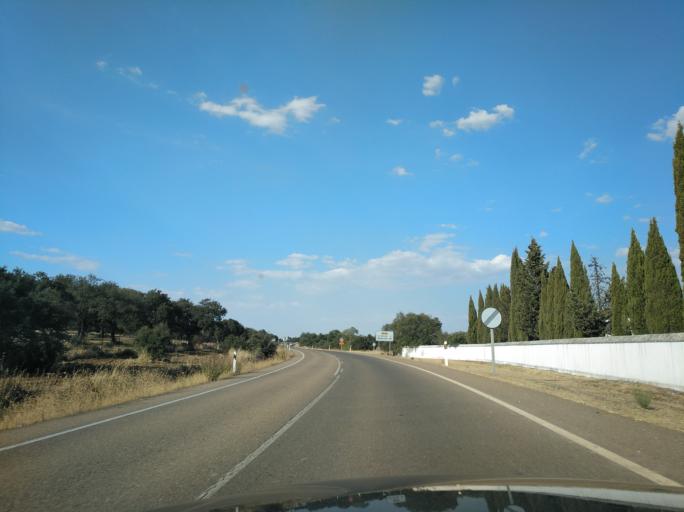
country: ES
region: Extremadura
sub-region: Provincia de Badajoz
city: Villanueva del Fresno
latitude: 38.3838
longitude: -7.1537
